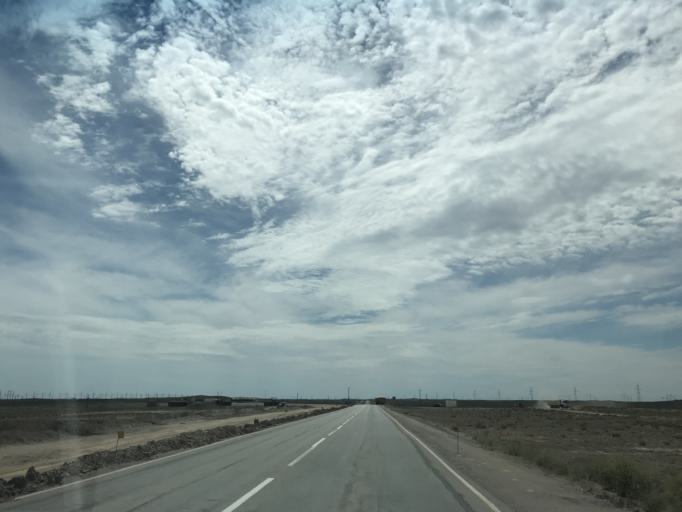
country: KZ
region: Almaty Oblysy
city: Ulken
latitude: 45.2357
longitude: 73.8347
